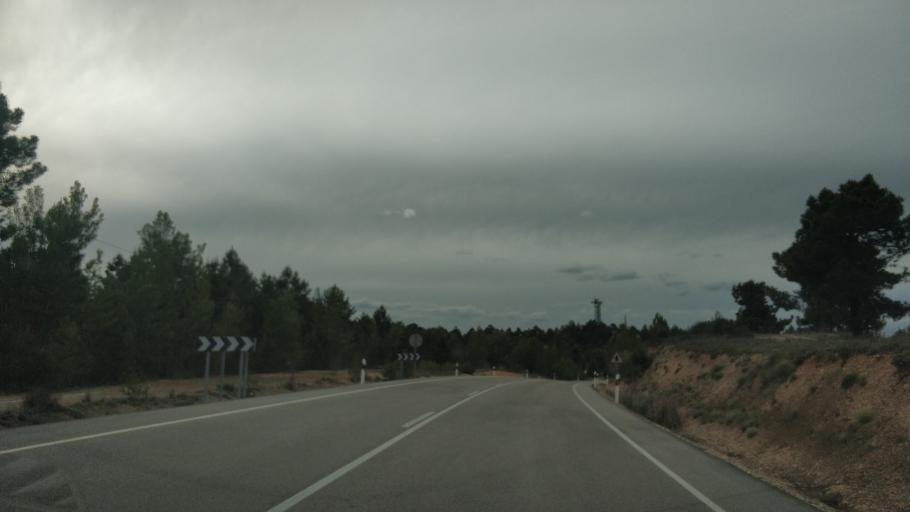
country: ES
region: Castille and Leon
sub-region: Provincia de Soria
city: Quintanas de Gormaz
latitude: 41.5310
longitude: -2.9478
